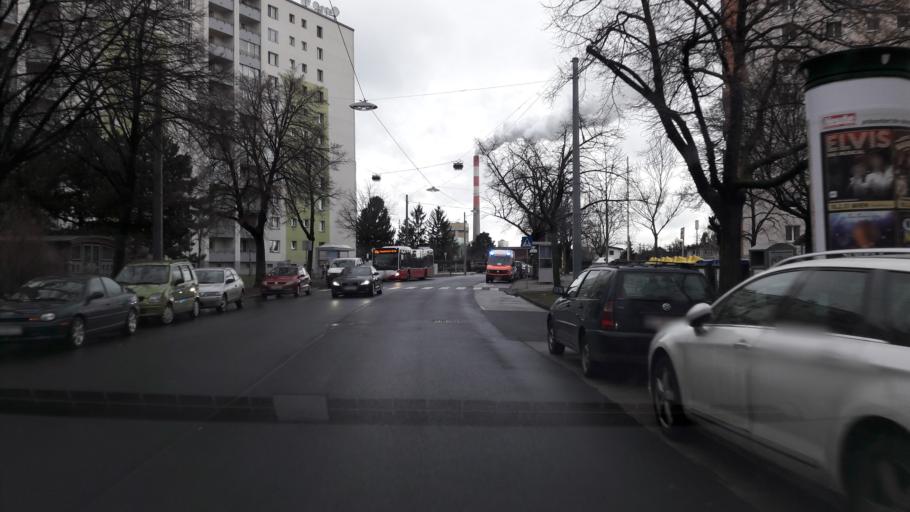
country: AT
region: Lower Austria
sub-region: Politischer Bezirk Wien-Umgebung
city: Schwechat
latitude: 48.1691
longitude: 16.4320
